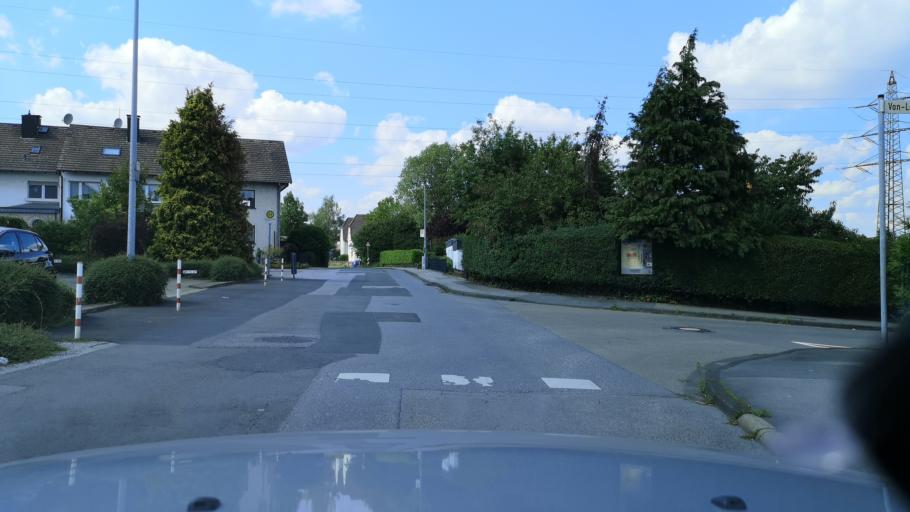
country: DE
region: North Rhine-Westphalia
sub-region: Regierungsbezirk Arnsberg
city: Menden
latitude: 51.4478
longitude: 7.7737
